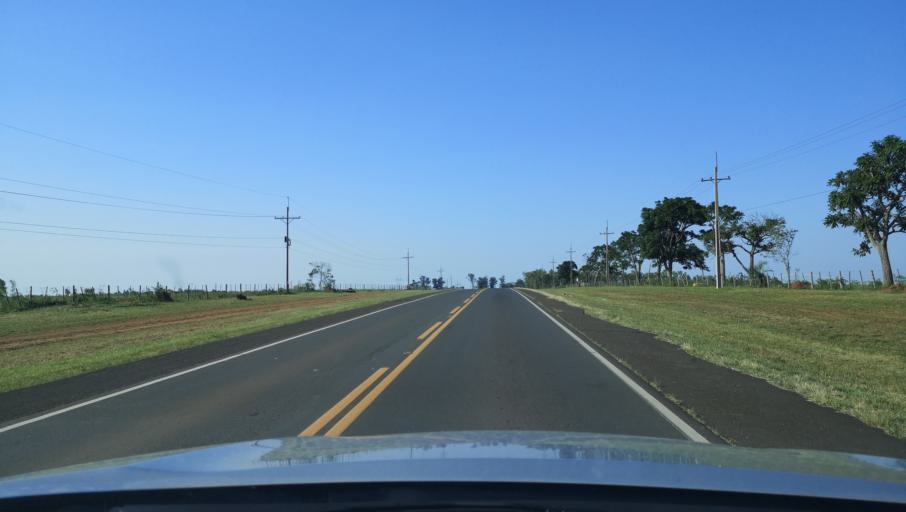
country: PY
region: Misiones
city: Santa Maria
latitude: -26.8133
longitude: -57.0230
